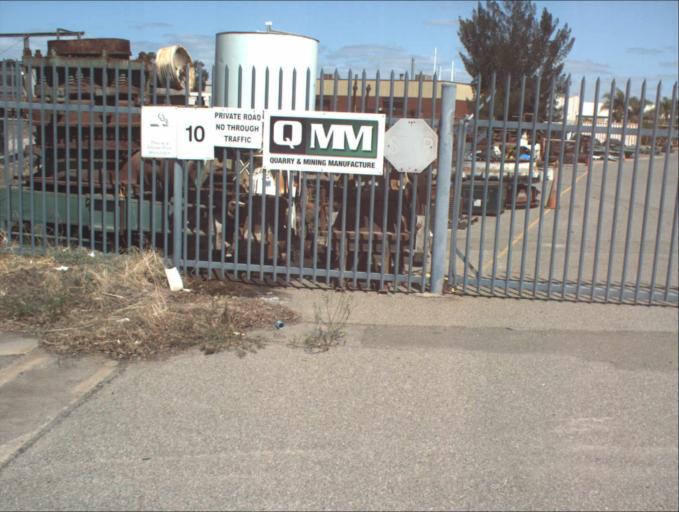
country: AU
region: South Australia
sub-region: Port Adelaide Enfield
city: Alberton
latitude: -34.8476
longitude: 138.5427
